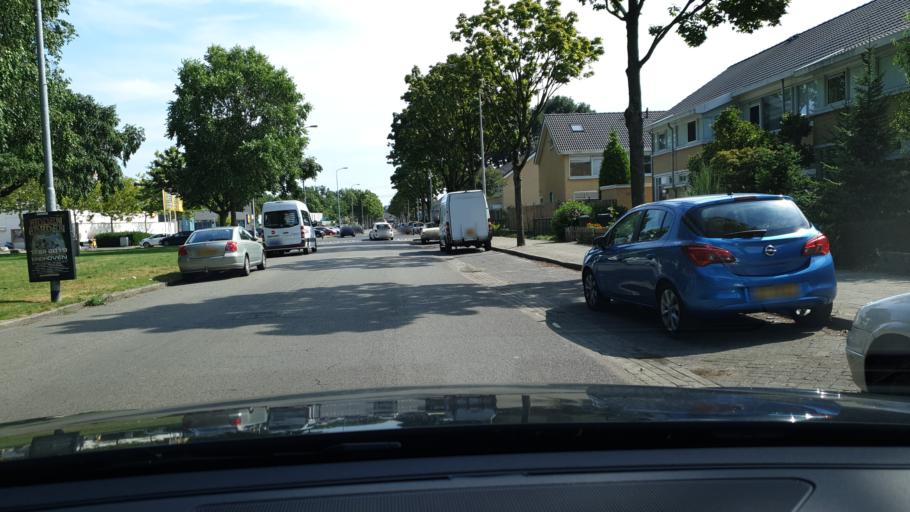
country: NL
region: North Brabant
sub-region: Gemeente Eindhoven
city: Eindhoven
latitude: 51.4799
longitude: 5.4615
